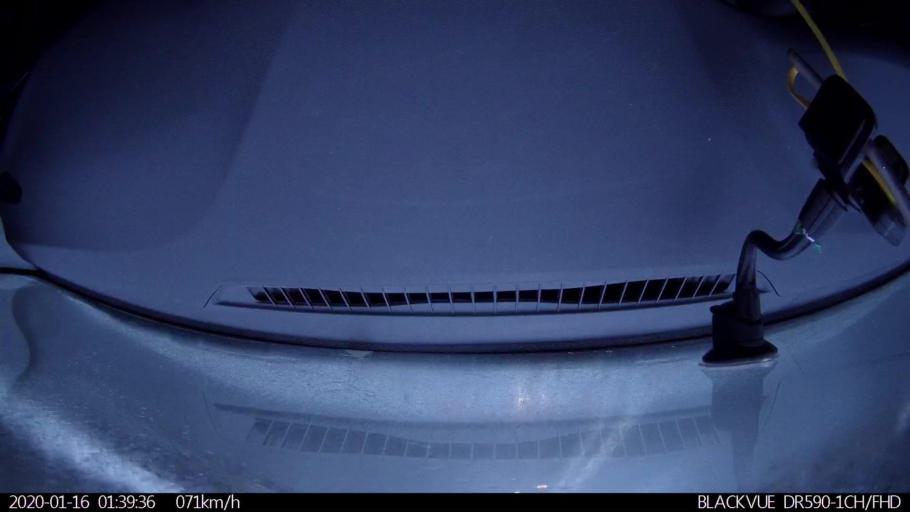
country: RU
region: Nizjnij Novgorod
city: Gorbatovka
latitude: 56.3334
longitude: 43.7934
